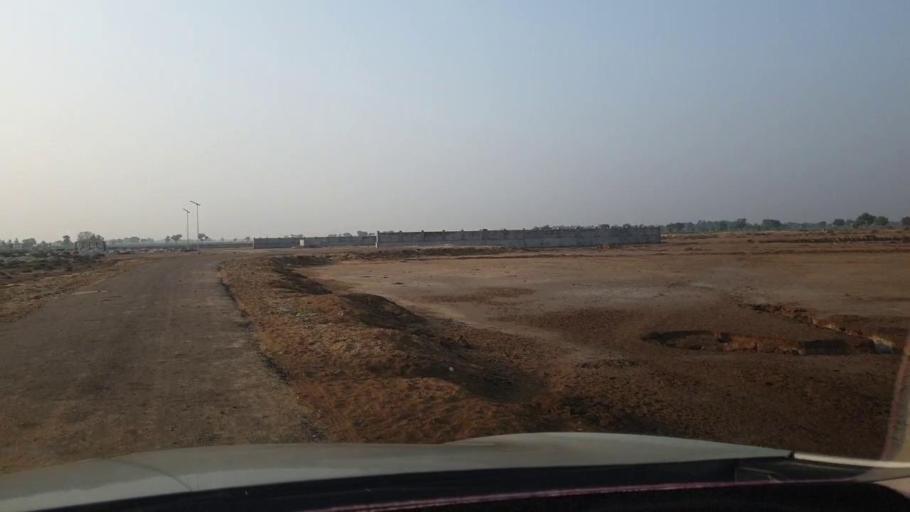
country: PK
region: Sindh
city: Sehwan
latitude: 26.3520
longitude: 67.7610
